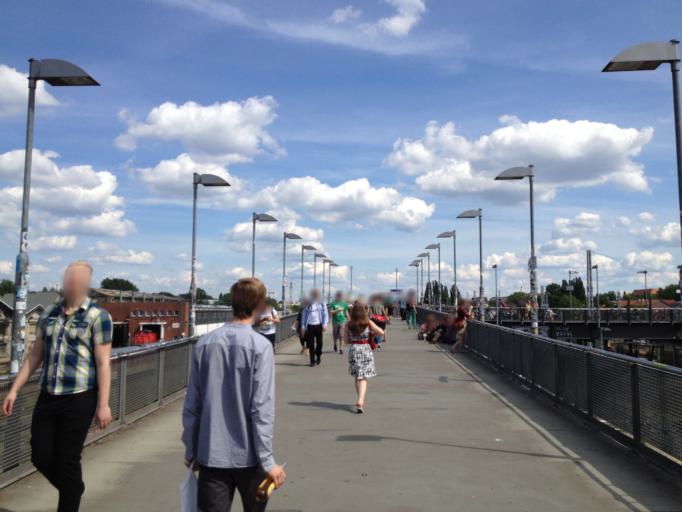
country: DE
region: Berlin
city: Friedrichshain Bezirk
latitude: 52.5066
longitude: 13.4504
